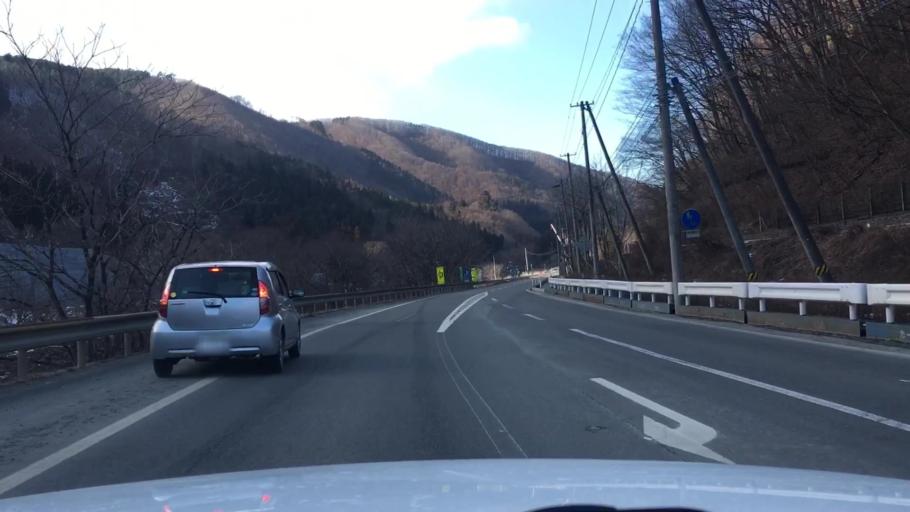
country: JP
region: Iwate
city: Miyako
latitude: 39.6089
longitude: 141.6353
